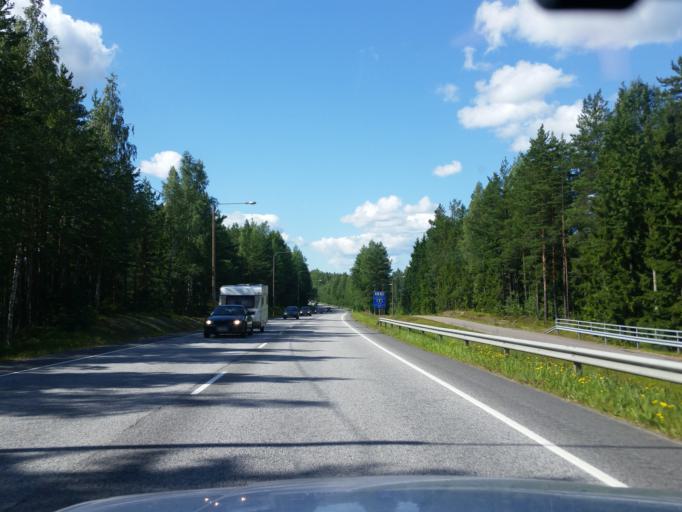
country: FI
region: Uusimaa
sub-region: Helsinki
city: Vihti
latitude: 60.3140
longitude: 24.2501
